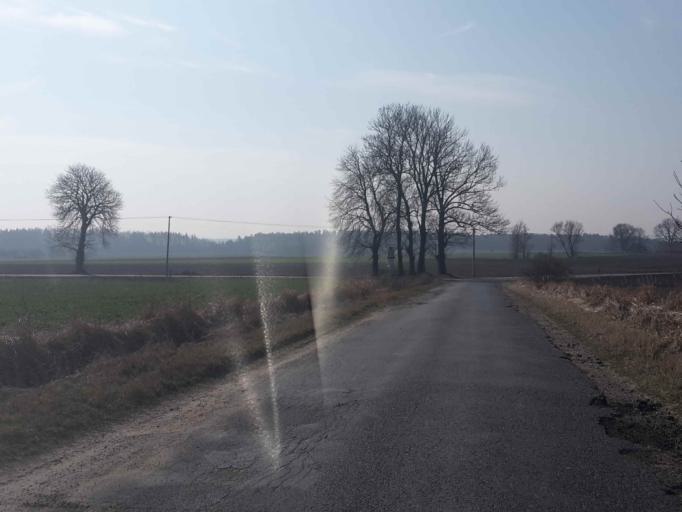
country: PL
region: Kujawsko-Pomorskie
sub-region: Powiat rypinski
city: Wapielsk
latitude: 53.2034
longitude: 19.2360
